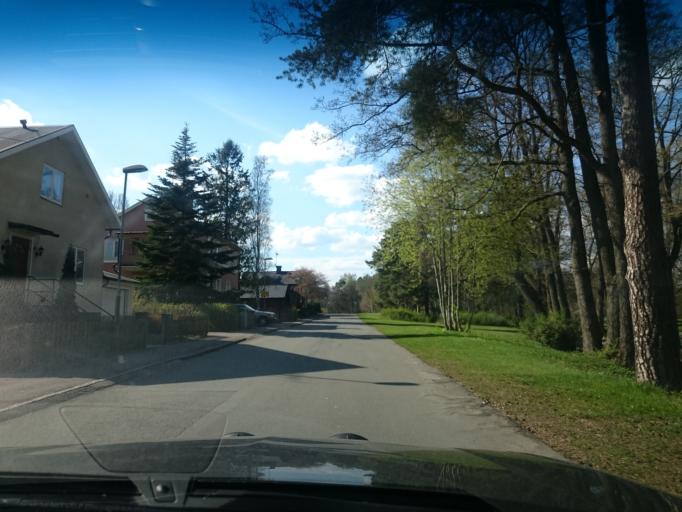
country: SE
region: Joenkoeping
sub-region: Vetlanda Kommun
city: Vetlanda
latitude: 57.4309
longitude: 15.0820
